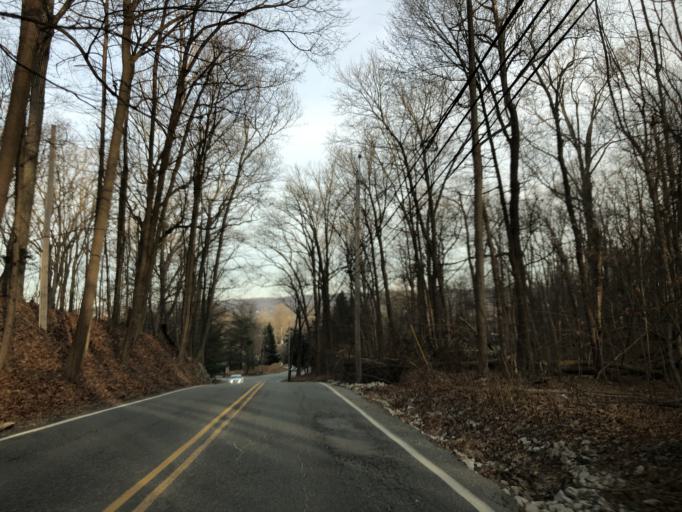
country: US
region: Pennsylvania
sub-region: Chester County
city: Exton
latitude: 40.0201
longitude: -75.6077
